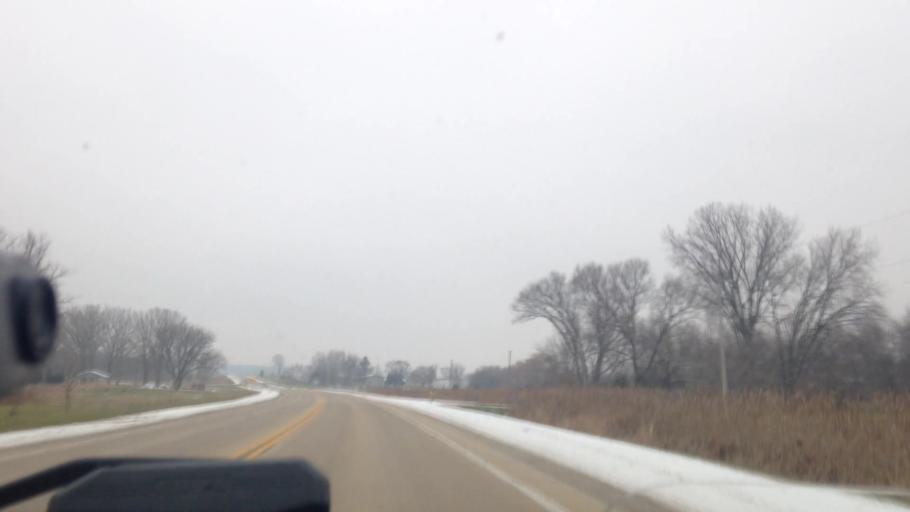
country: US
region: Wisconsin
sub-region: Dodge County
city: Mayville
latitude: 43.4833
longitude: -88.5457
